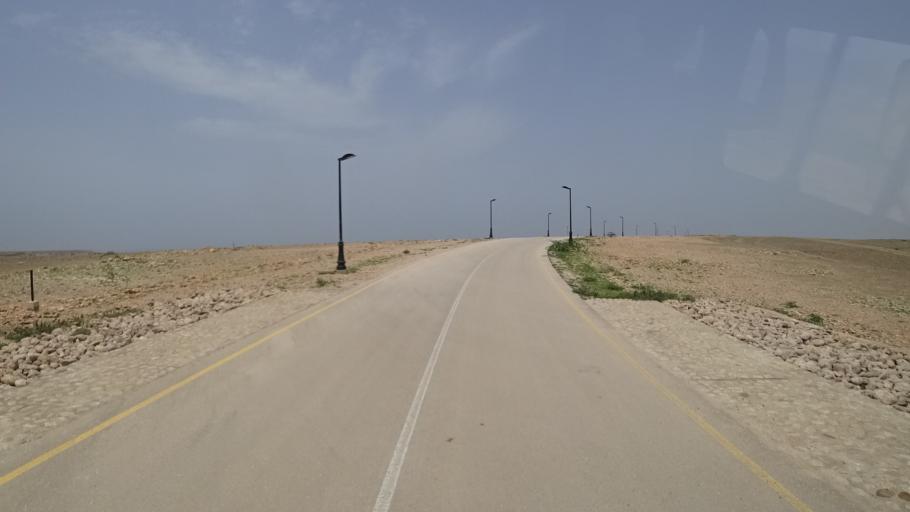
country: OM
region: Zufar
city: Salalah
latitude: 17.0492
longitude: 54.4369
